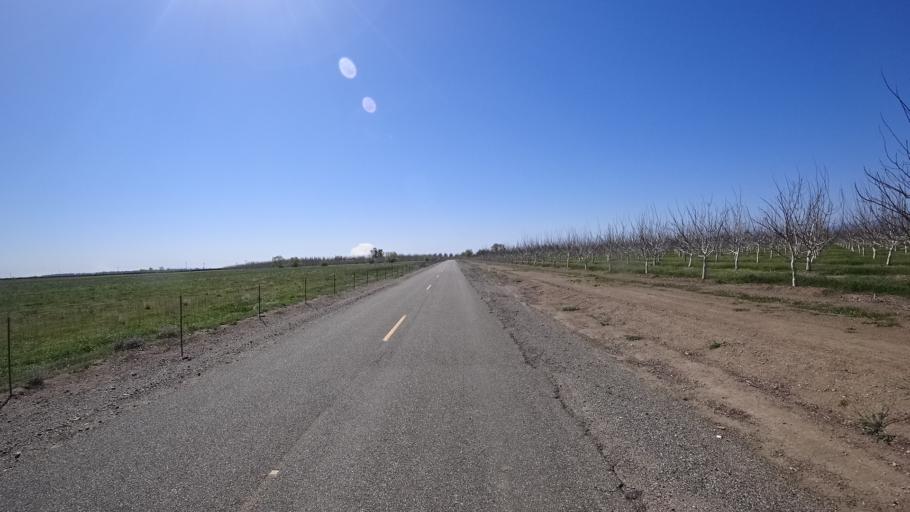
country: US
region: California
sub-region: Glenn County
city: Willows
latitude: 39.6283
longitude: -122.2535
